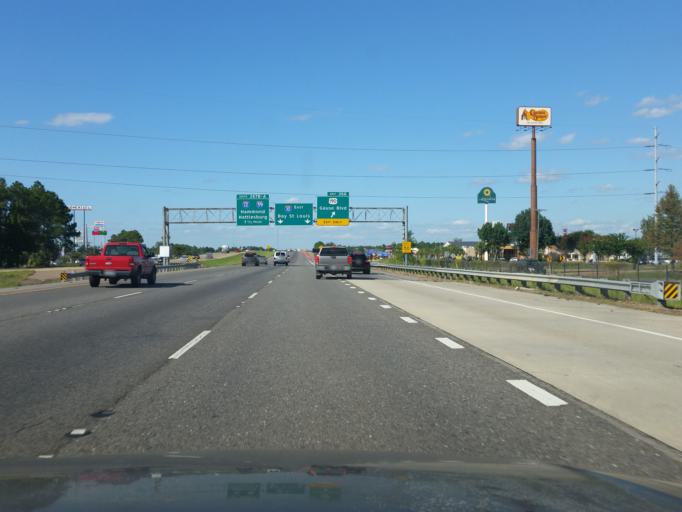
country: US
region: Louisiana
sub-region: Saint Tammany Parish
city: Slidell
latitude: 30.2804
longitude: -89.7510
